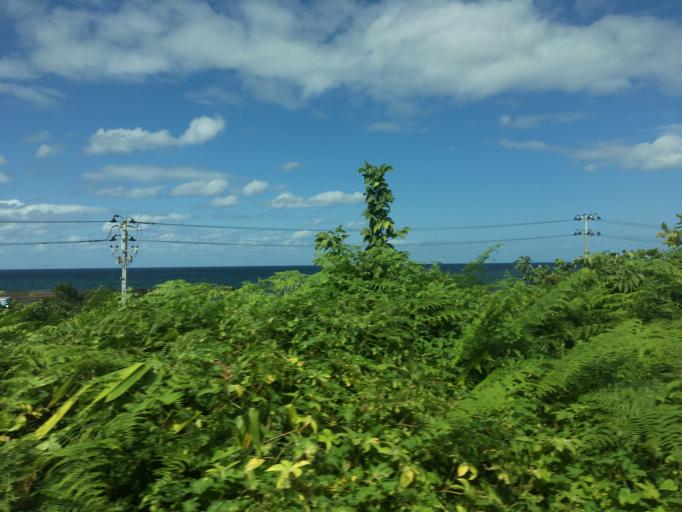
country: JP
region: Aomori
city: Shimokizukuri
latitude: 40.7702
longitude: 140.1733
